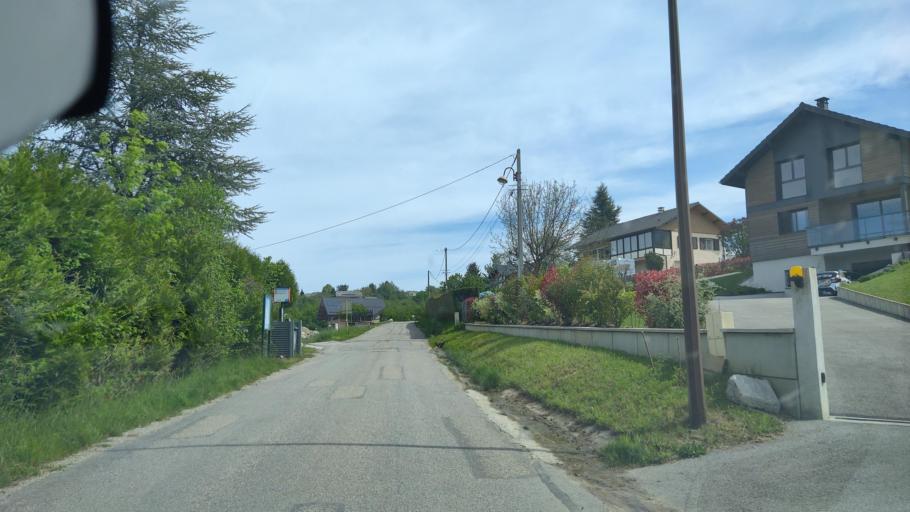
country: FR
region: Rhone-Alpes
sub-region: Departement de la Savoie
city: Mouxy
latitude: 45.6985
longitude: 5.9505
